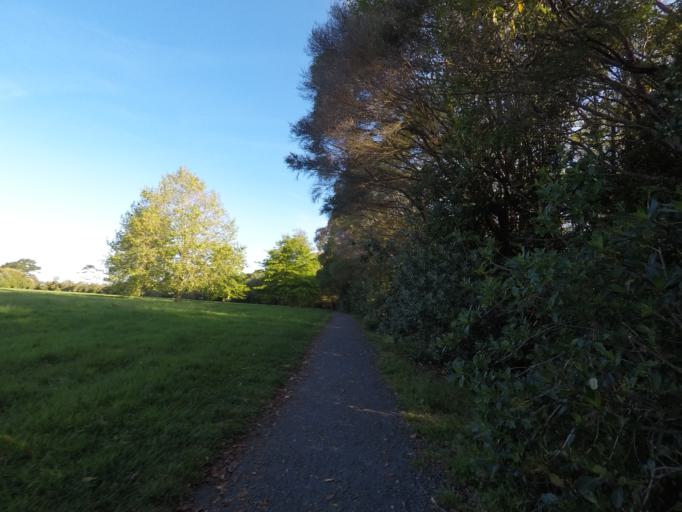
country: NZ
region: Auckland
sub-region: Auckland
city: Rosebank
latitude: -36.8423
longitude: 174.6334
